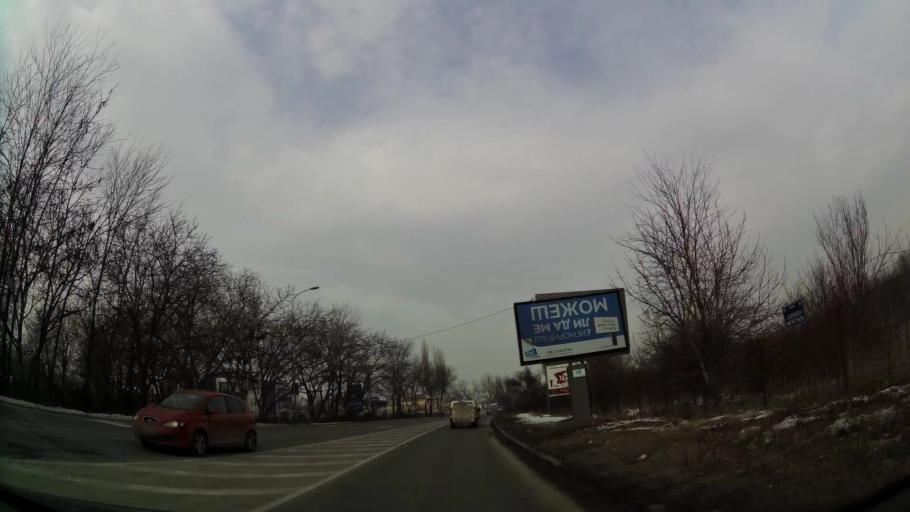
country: MK
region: Suto Orizari
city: Suto Orizare
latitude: 42.0164
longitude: 21.4113
